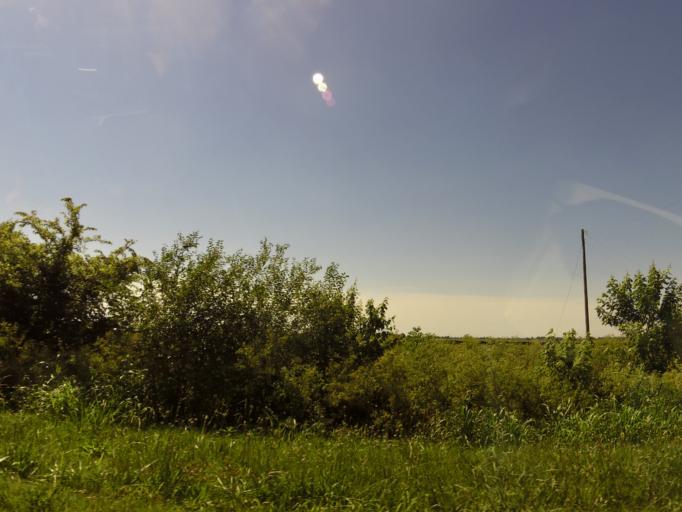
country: US
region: Missouri
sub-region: Dunklin County
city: Campbell
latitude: 36.4787
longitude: -90.0986
